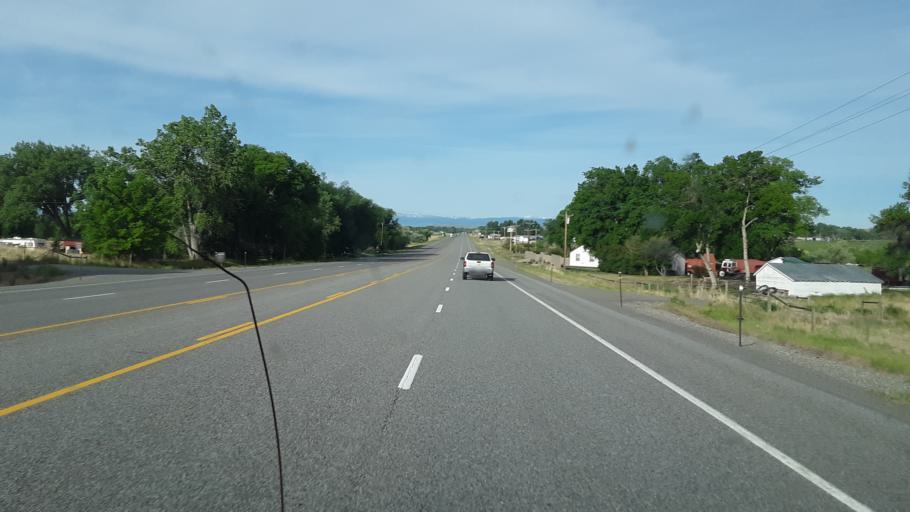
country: US
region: Wyoming
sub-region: Fremont County
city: Riverton
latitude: 43.1197
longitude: -108.3241
